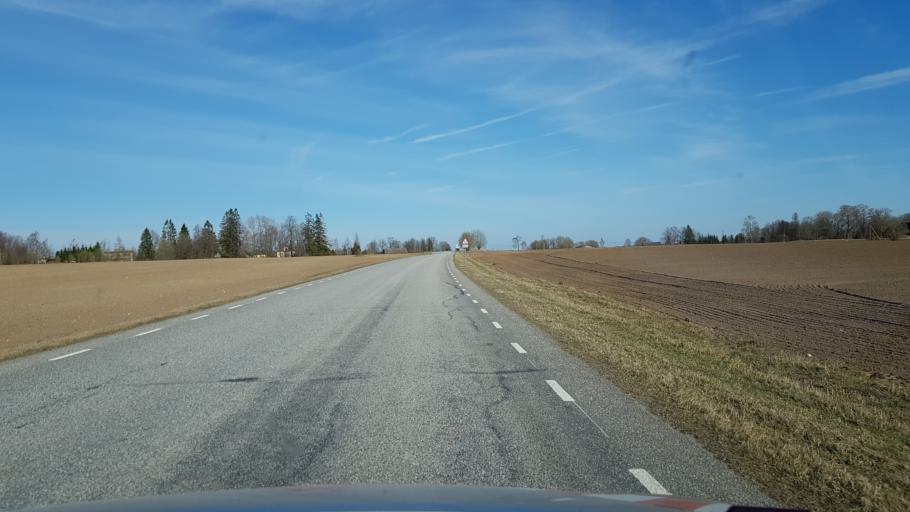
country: EE
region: Laeaene-Virumaa
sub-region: Vinni vald
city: Vinni
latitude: 59.0697
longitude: 26.5180
